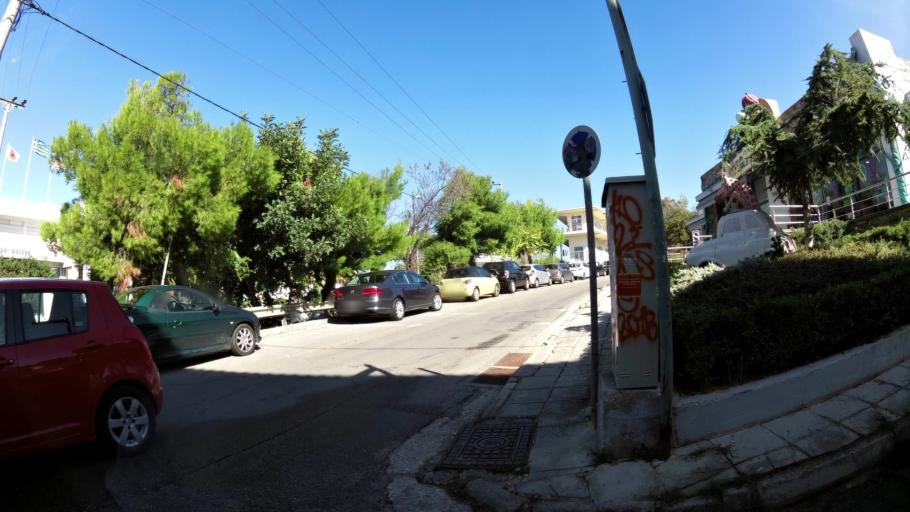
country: GR
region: Attica
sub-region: Nomarchia Anatolikis Attikis
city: Anoixi
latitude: 38.1295
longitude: 23.8579
